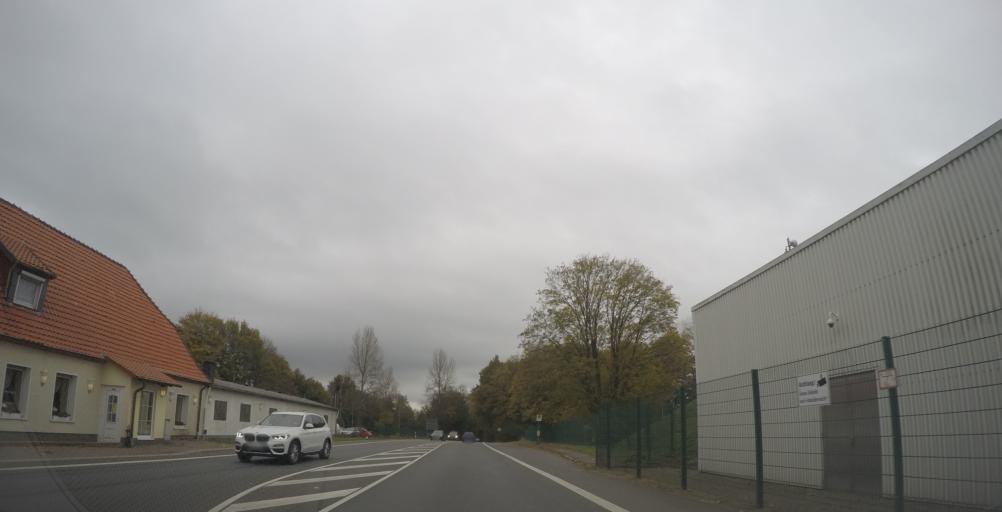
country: DE
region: North Rhine-Westphalia
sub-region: Regierungsbezirk Arnsberg
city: Unna
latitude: 51.4998
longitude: 7.7035
